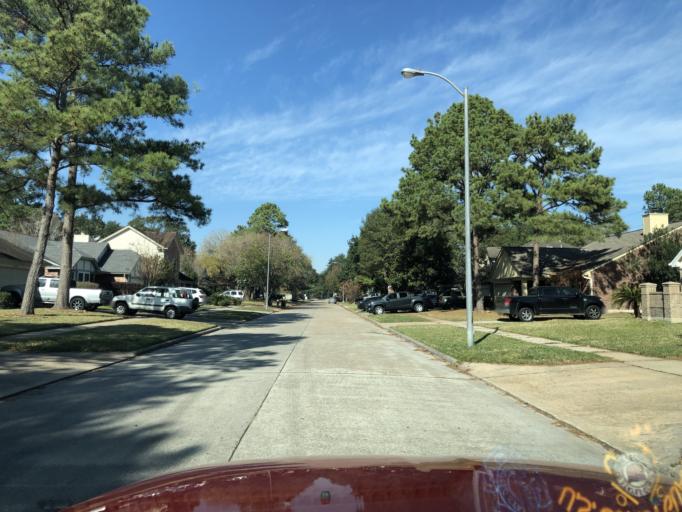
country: US
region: Texas
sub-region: Harris County
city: Tomball
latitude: 30.0188
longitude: -95.5556
